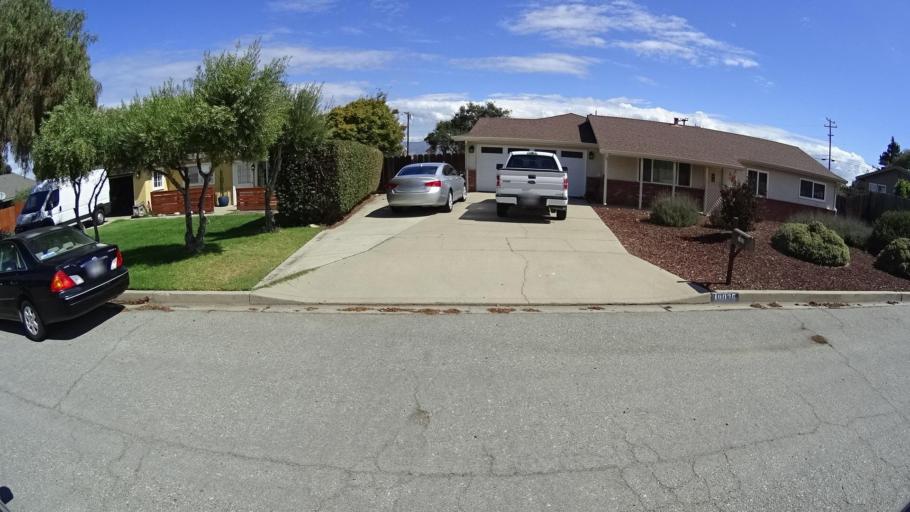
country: US
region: California
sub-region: Monterey County
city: Salinas
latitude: 36.6001
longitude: -121.6273
